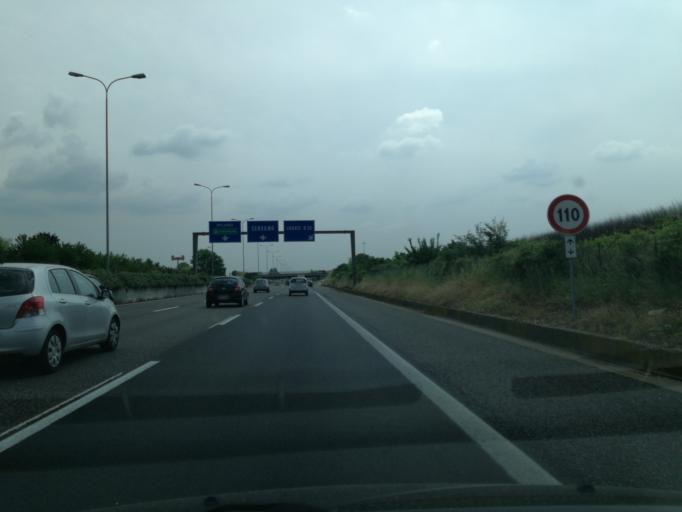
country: IT
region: Lombardy
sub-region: Provincia di Monza e Brianza
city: Carate Brianza
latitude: 45.6704
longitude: 9.2208
